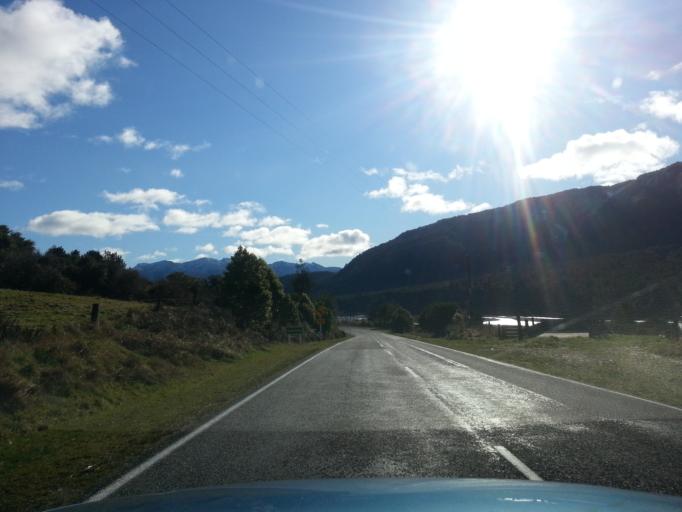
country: NZ
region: West Coast
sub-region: Grey District
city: Greymouth
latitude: -42.7457
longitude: 171.5296
